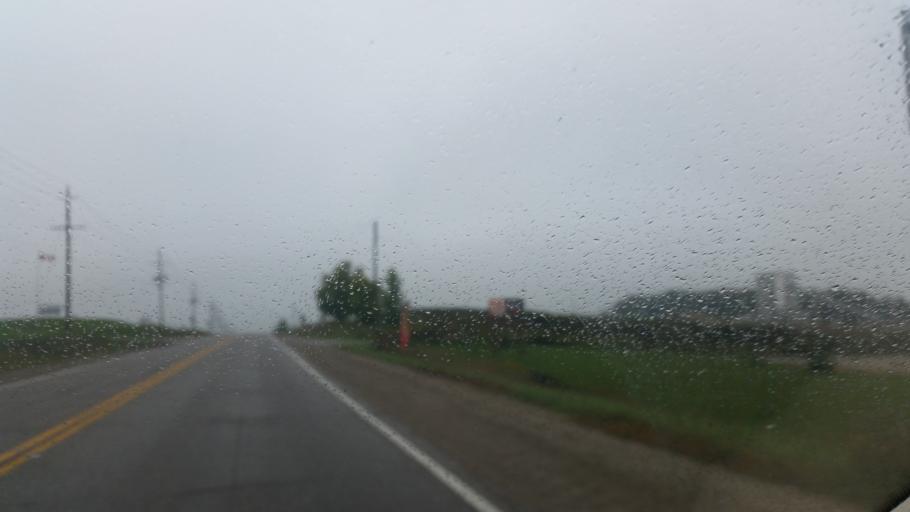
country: CA
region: Ontario
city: Waterloo
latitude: 43.6897
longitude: -80.4508
